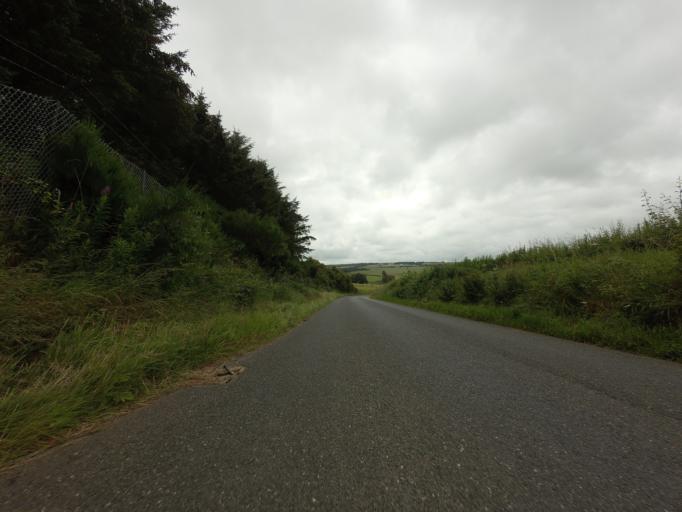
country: GB
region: Scotland
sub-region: Aberdeenshire
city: Turriff
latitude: 57.5334
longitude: -2.4019
